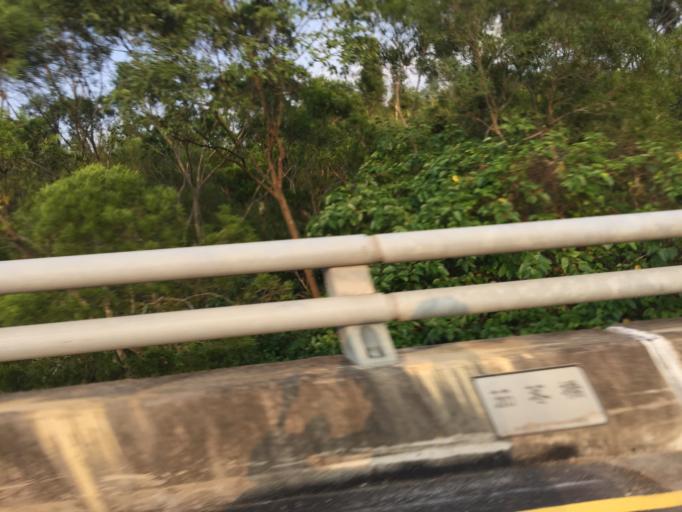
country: TW
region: Taiwan
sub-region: Hsinchu
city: Hsinchu
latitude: 24.7643
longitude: 120.9572
